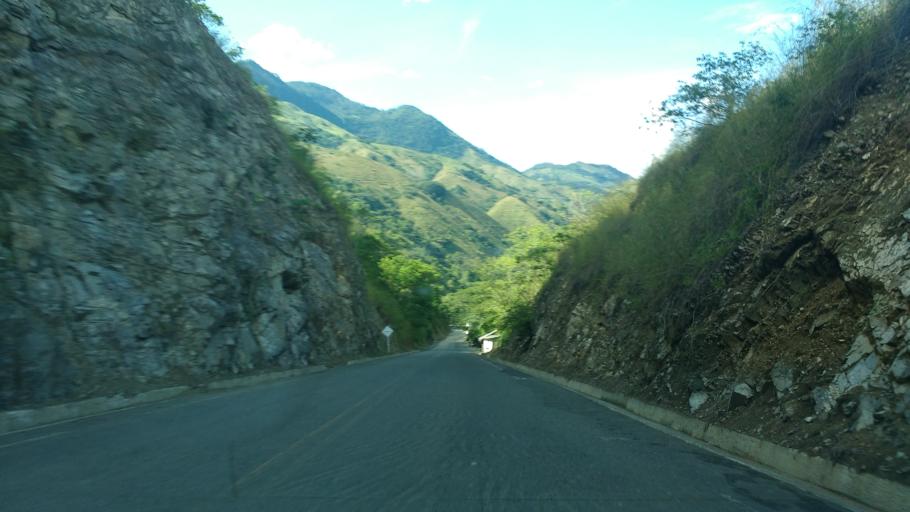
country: CO
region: Antioquia
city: Concordia
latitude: 6.0388
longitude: -75.8601
